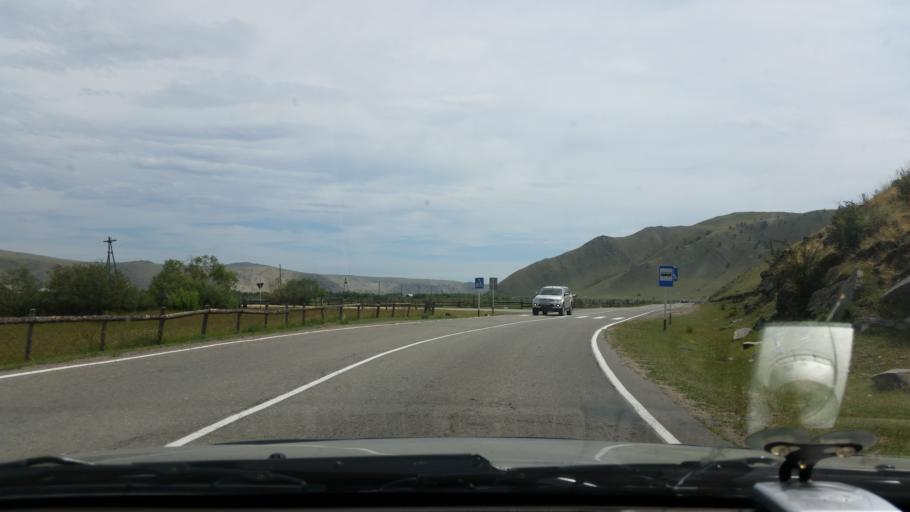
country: RU
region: Irkutsk
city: Yelantsy
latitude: 52.8068
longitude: 106.4648
